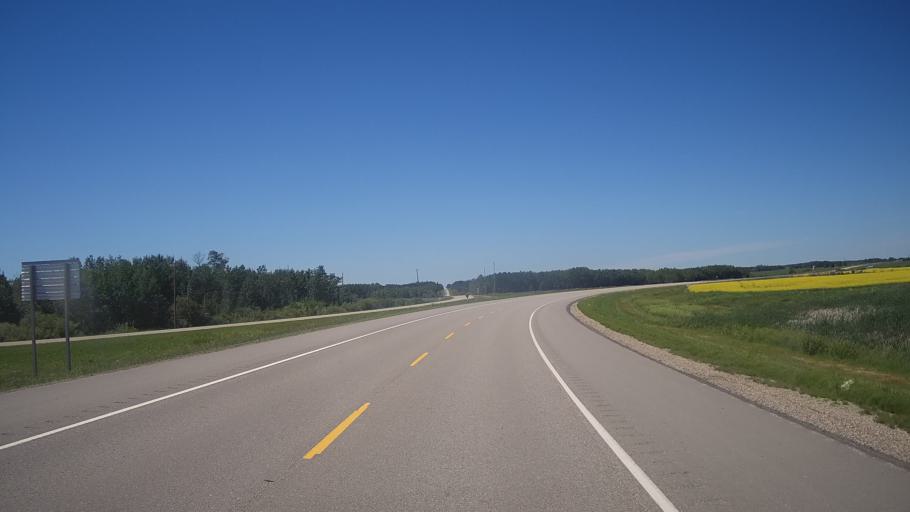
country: CA
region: Manitoba
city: Minnedosa
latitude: 50.2699
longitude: -99.9311
